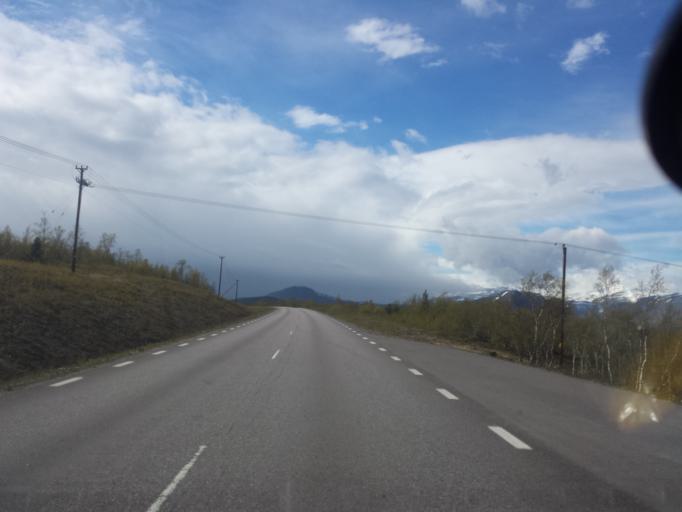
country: SE
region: Norrbotten
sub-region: Kiruna Kommun
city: Kiruna
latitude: 68.2153
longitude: 19.7405
